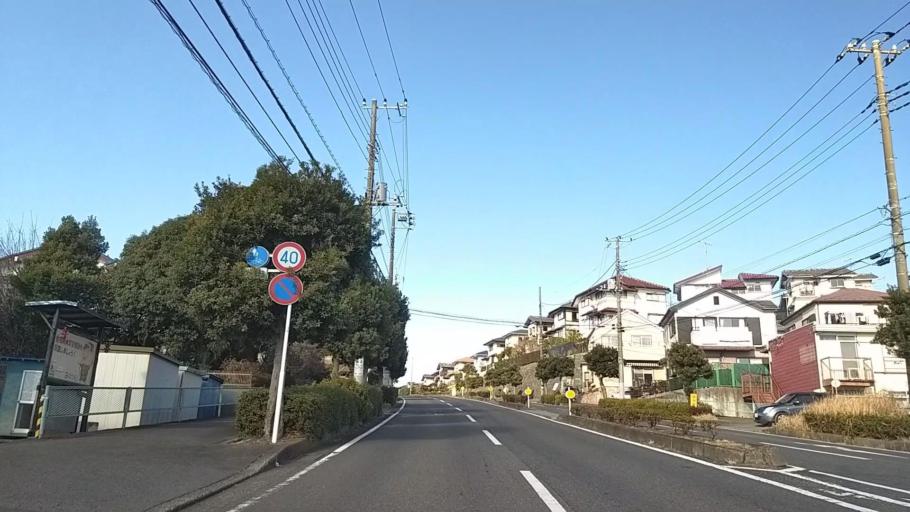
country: JP
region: Kanagawa
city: Atsugi
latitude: 35.4342
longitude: 139.3308
